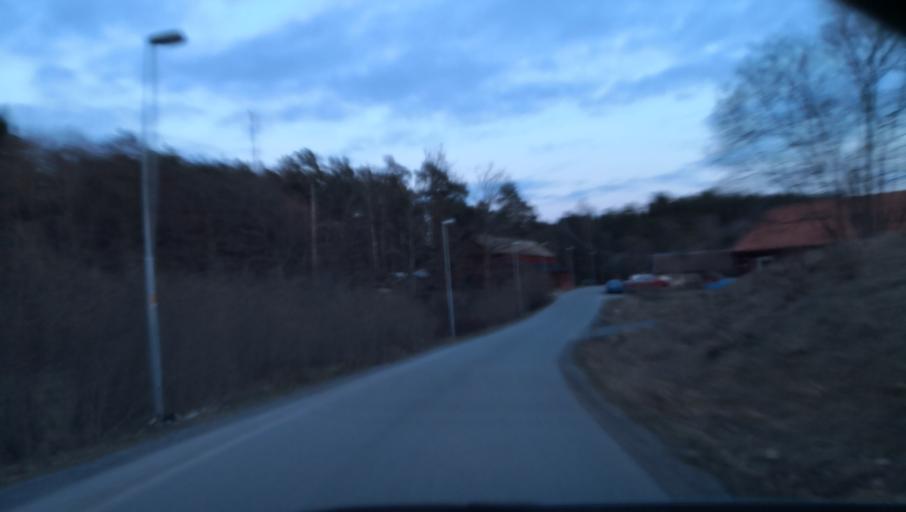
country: SE
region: Stockholm
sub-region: Nacka Kommun
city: Boo
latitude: 59.3315
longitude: 18.3151
